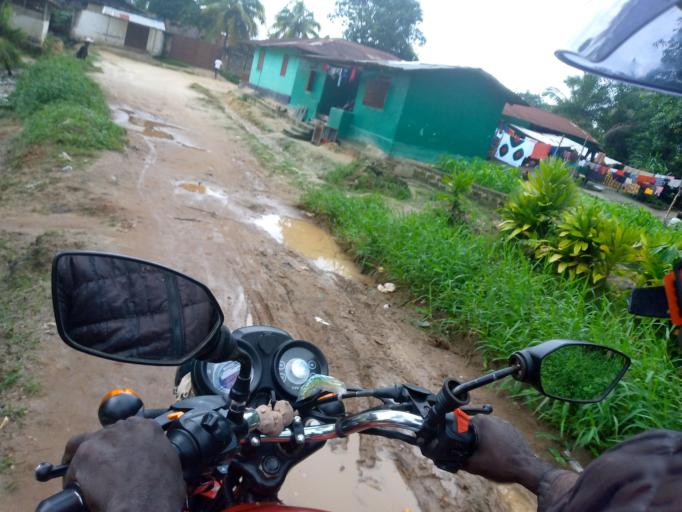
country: SL
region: Eastern Province
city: Kenema
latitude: 7.8772
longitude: -11.1803
